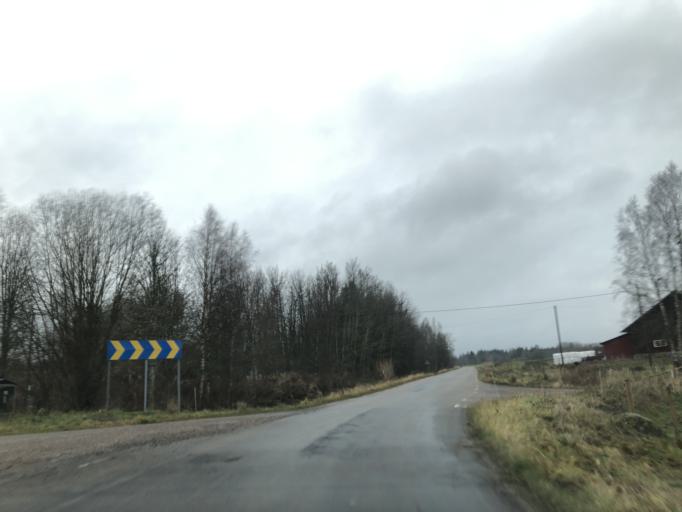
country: SE
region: Vaestra Goetaland
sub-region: Ulricehamns Kommun
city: Ulricehamn
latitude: 57.8826
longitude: 13.5153
